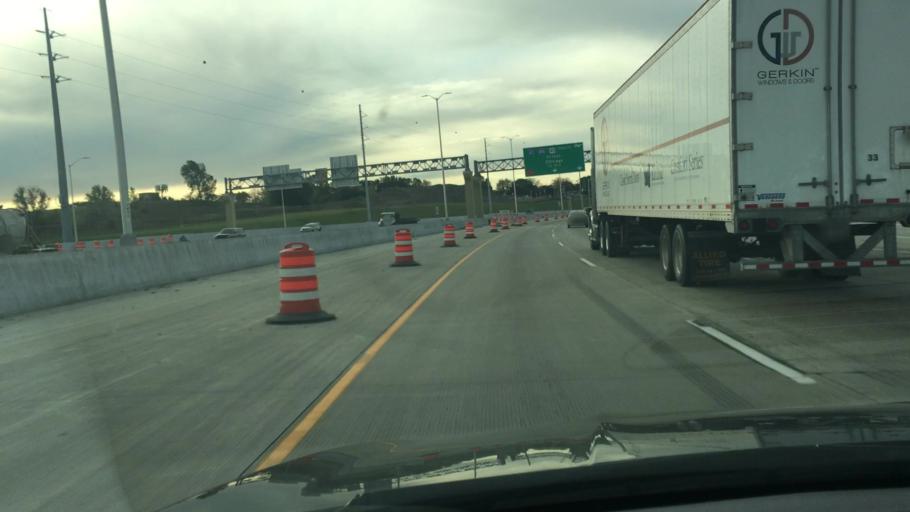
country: US
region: Wisconsin
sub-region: Milwaukee County
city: Wauwatosa
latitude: 43.0427
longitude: -88.0340
